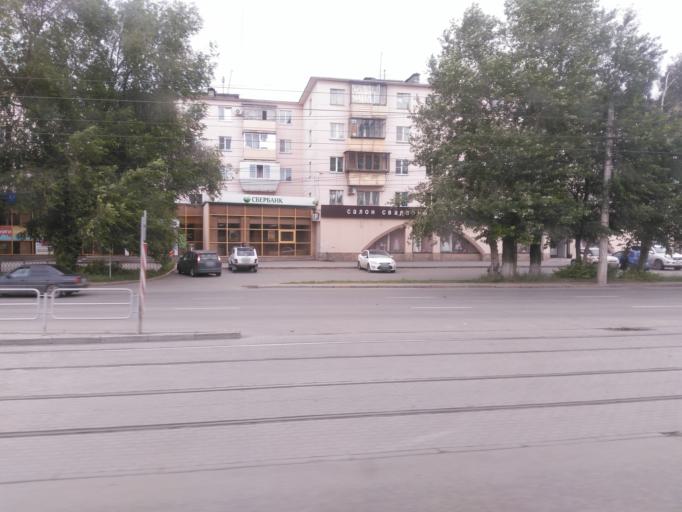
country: RU
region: Chelyabinsk
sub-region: Gorod Chelyabinsk
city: Chelyabinsk
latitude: 55.1831
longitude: 61.3988
